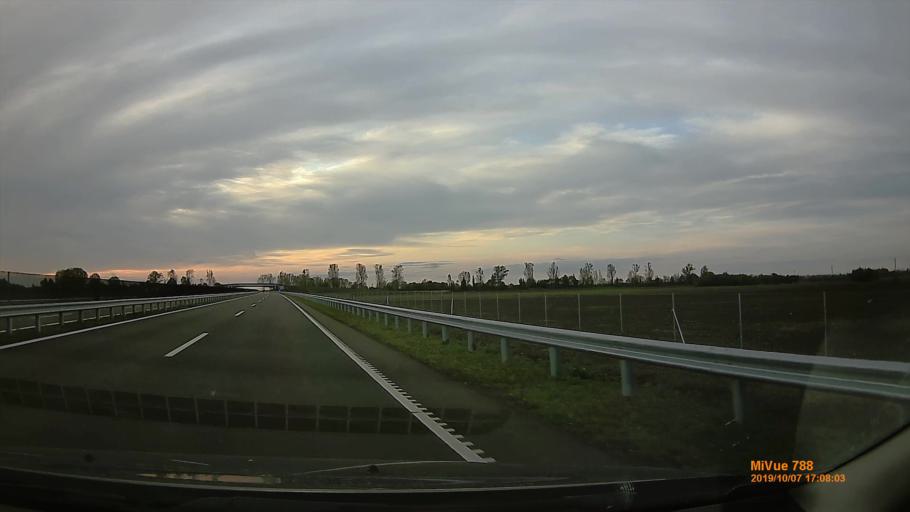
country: HU
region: Bekes
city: Bekesszentandras
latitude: 46.8240
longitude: 20.4974
